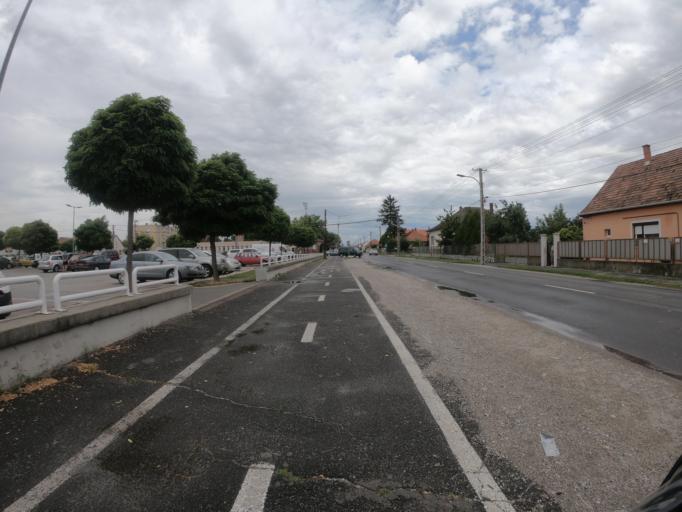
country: HU
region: Borsod-Abauj-Zemplen
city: Mezokovesd
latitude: 47.8001
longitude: 20.5698
